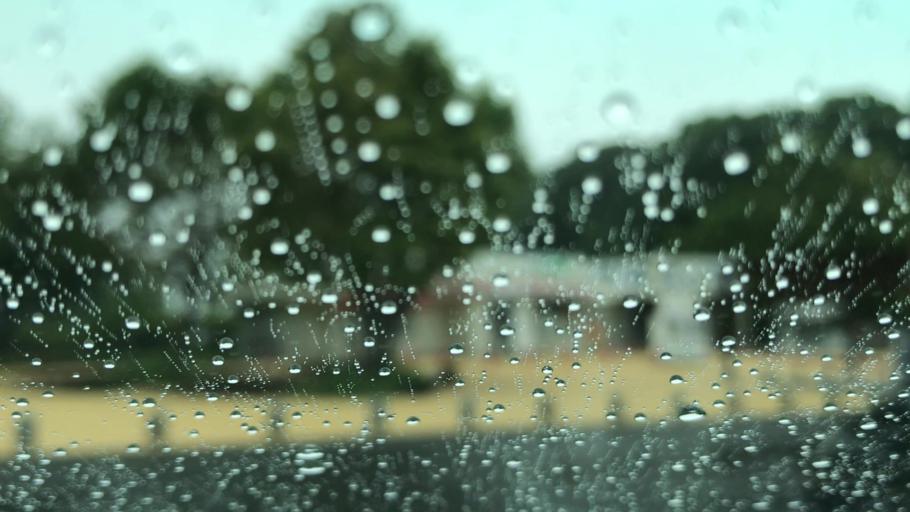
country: JP
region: Hokkaido
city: Shiraoi
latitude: 42.6105
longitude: 141.4647
